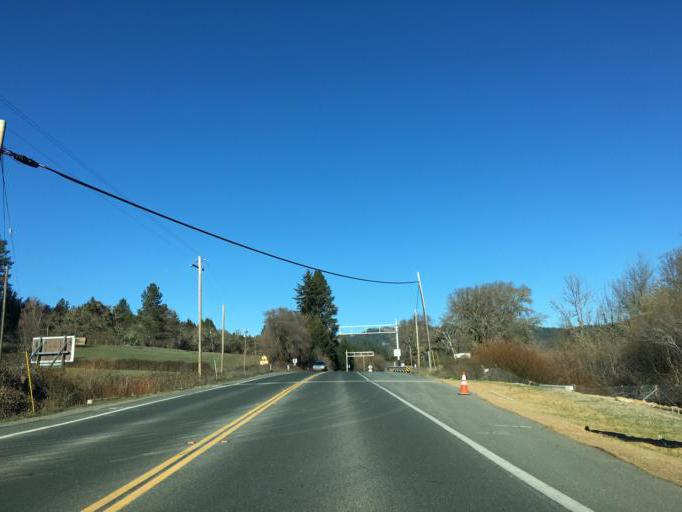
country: US
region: California
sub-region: Mendocino County
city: Brooktrails
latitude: 39.4392
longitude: -123.3561
